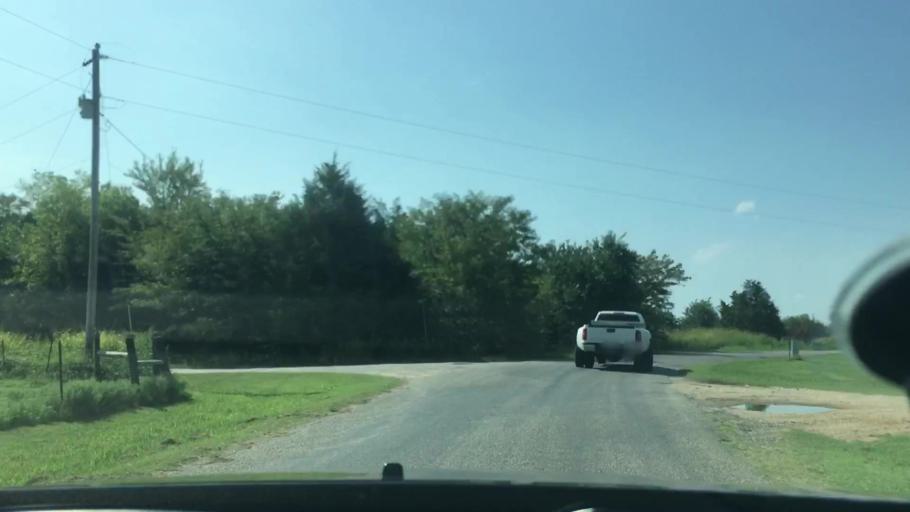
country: US
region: Oklahoma
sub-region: Bryan County
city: Colbert
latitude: 33.9061
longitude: -96.5378
